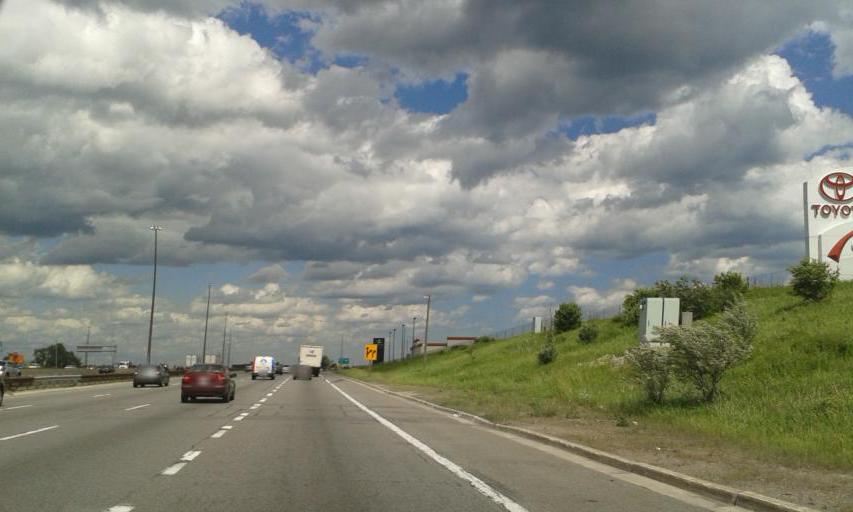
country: CA
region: Ontario
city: Scarborough
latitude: 43.7831
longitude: -79.2432
